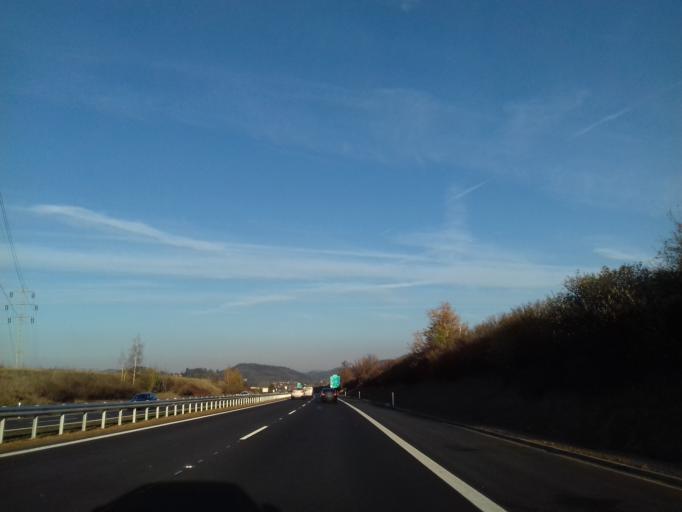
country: CZ
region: Central Bohemia
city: Zdice
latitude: 49.8961
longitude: 13.9503
